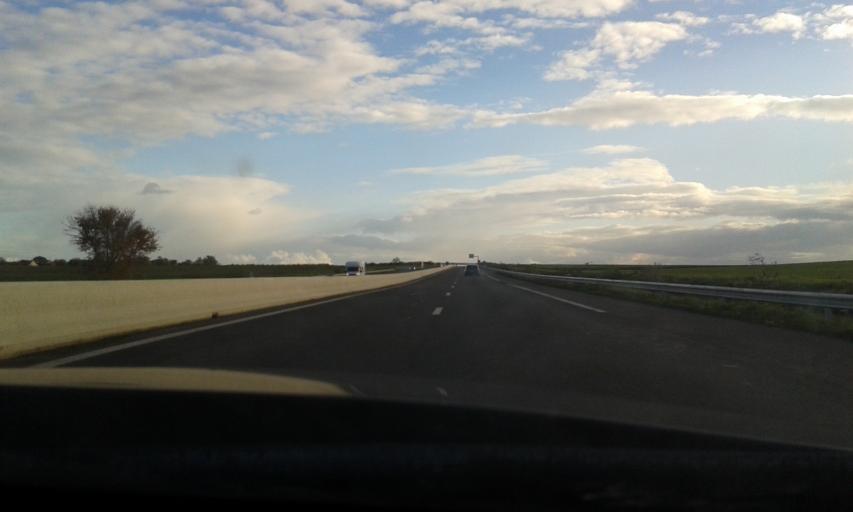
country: FR
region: Centre
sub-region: Departement d'Eure-et-Loir
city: Leves
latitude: 48.5146
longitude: 1.4604
